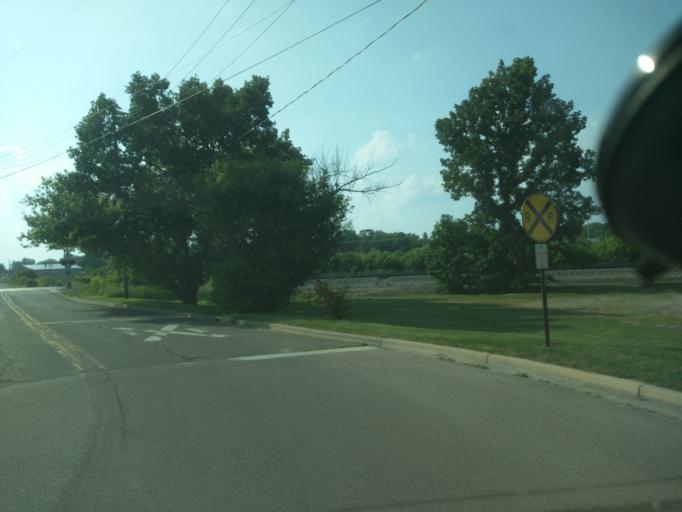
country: US
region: Michigan
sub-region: Jackson County
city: Jackson
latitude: 42.2525
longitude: -84.4313
